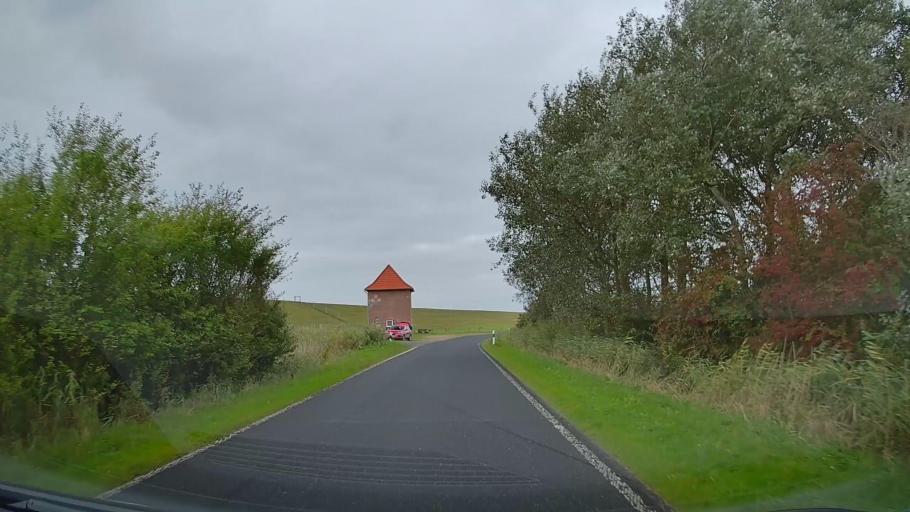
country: DE
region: Schleswig-Holstein
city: Emmelsbull-Horsbull
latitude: 54.8085
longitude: 8.6550
